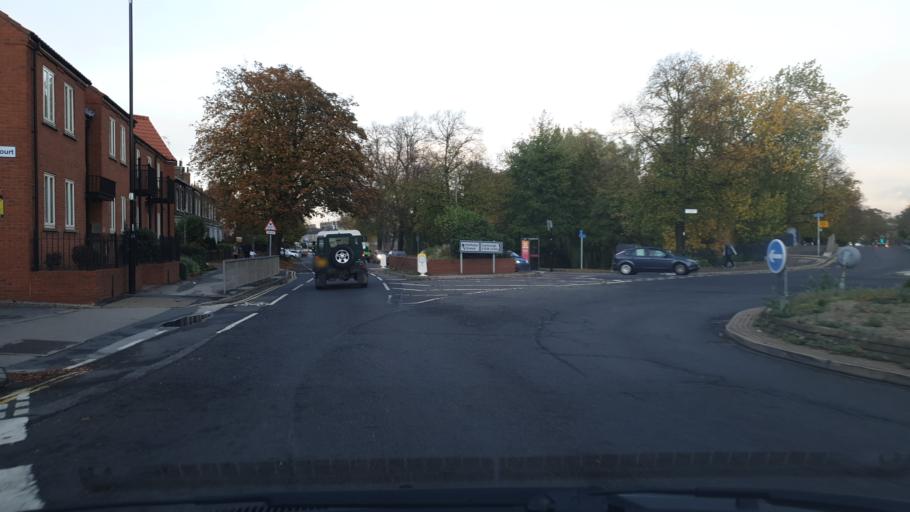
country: GB
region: England
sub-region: City of York
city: York
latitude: 53.9649
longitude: -1.0745
